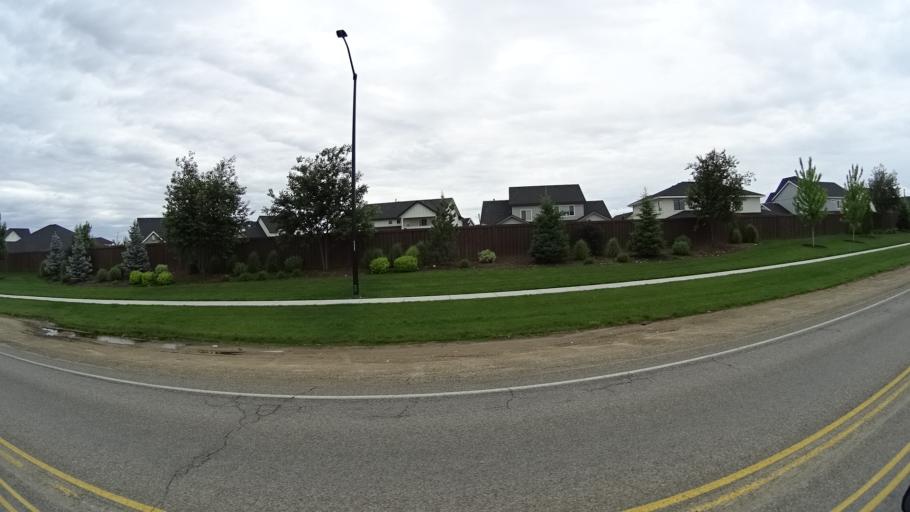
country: US
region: Idaho
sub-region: Ada County
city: Meridian
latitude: 43.6483
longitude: -116.4071
